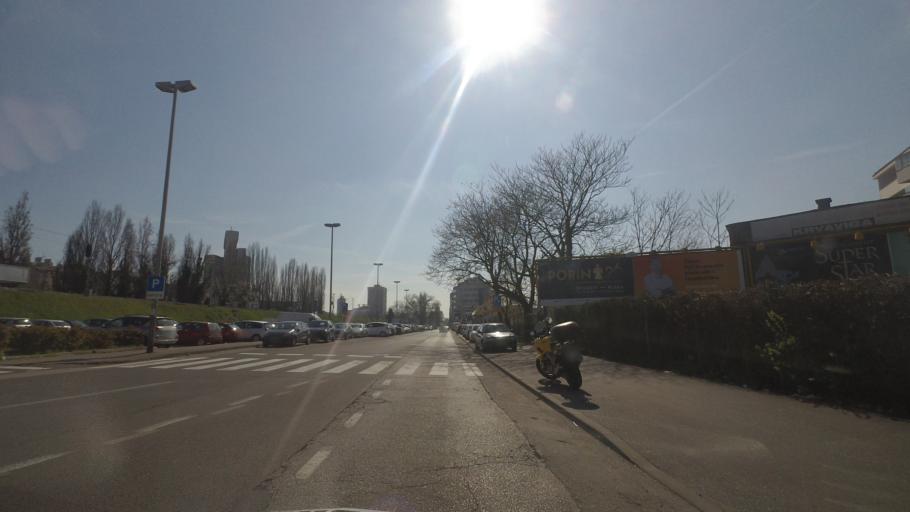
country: HR
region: Grad Zagreb
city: Zagreb - Centar
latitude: 45.8026
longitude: 15.9622
